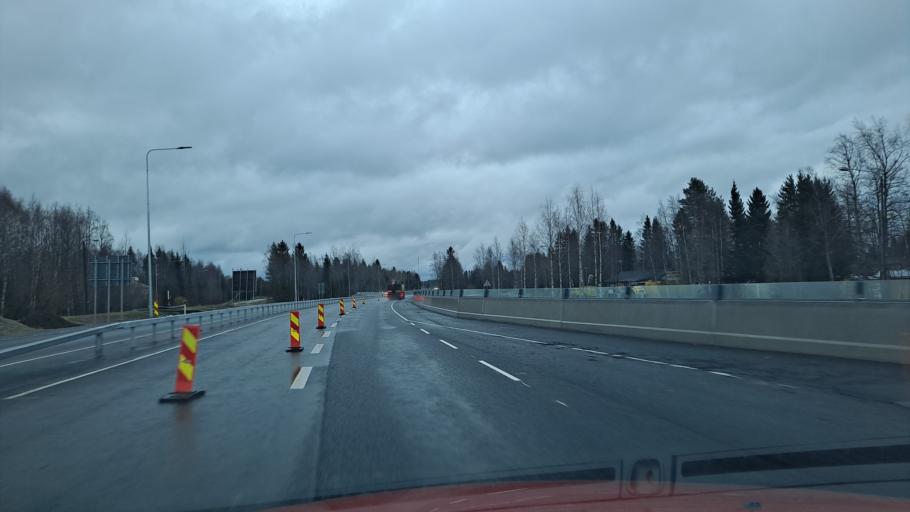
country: FI
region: Lapland
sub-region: Kemi-Tornio
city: Kemi
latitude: 65.6784
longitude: 24.7500
